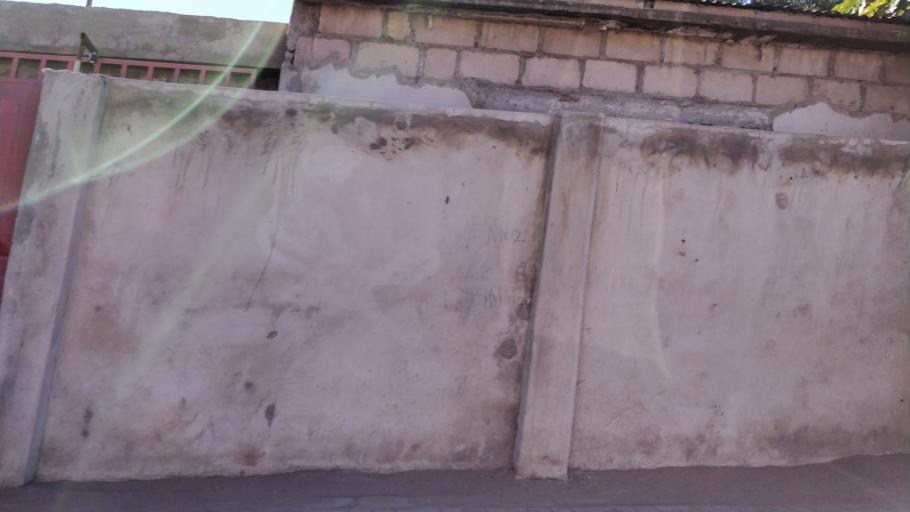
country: MZ
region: Maputo City
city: Maputo
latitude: -25.9303
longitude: 32.5985
